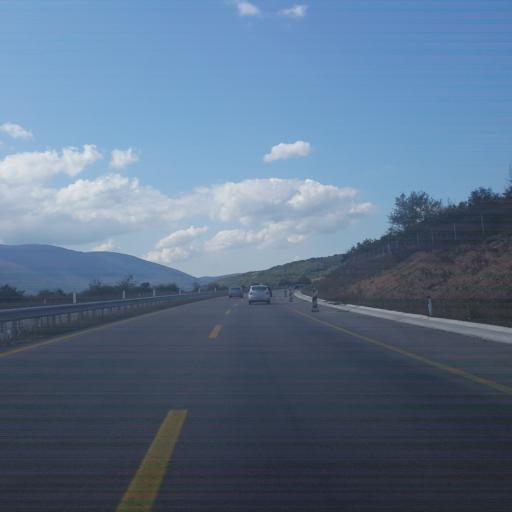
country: RS
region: Central Serbia
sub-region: Pirotski Okrug
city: Bela Palanka
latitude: 43.2354
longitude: 22.3544
